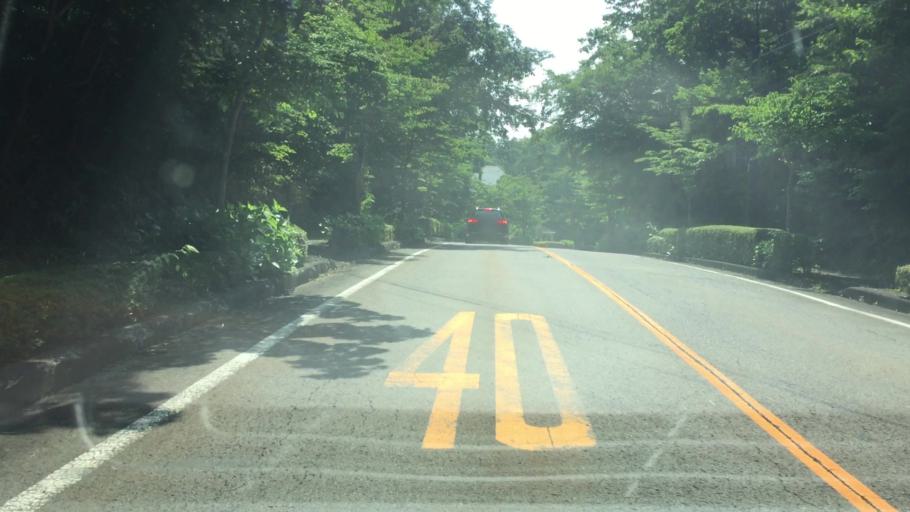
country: JP
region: Tochigi
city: Kuroiso
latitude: 37.1071
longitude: 140.0307
